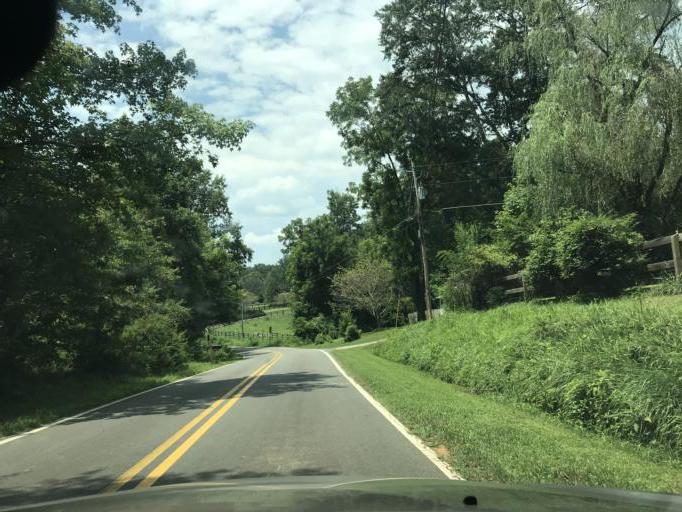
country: US
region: Georgia
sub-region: Dawson County
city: Dawsonville
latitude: 34.3315
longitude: -84.1975
